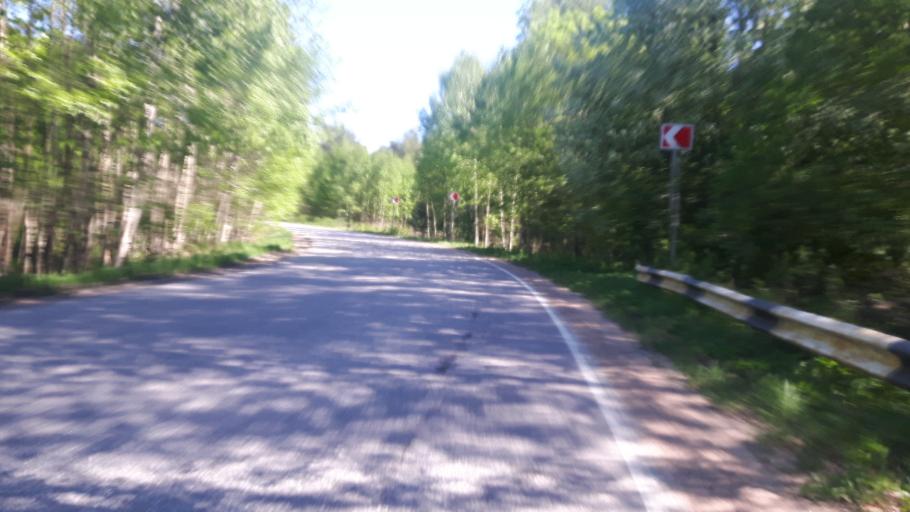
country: RU
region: Leningrad
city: Glebychevo
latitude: 60.2809
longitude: 28.8837
